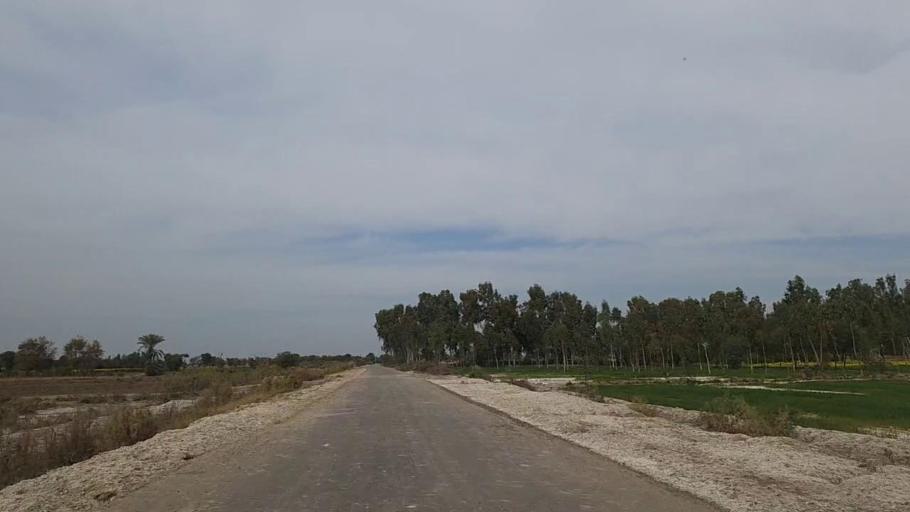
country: PK
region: Sindh
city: Daur
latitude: 26.4245
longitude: 68.4809
